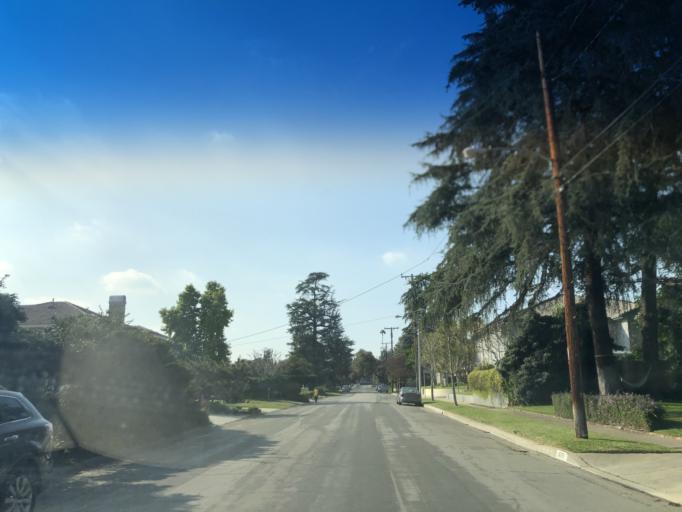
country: US
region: California
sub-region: Los Angeles County
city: East San Gabriel
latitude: 34.1110
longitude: -118.0860
